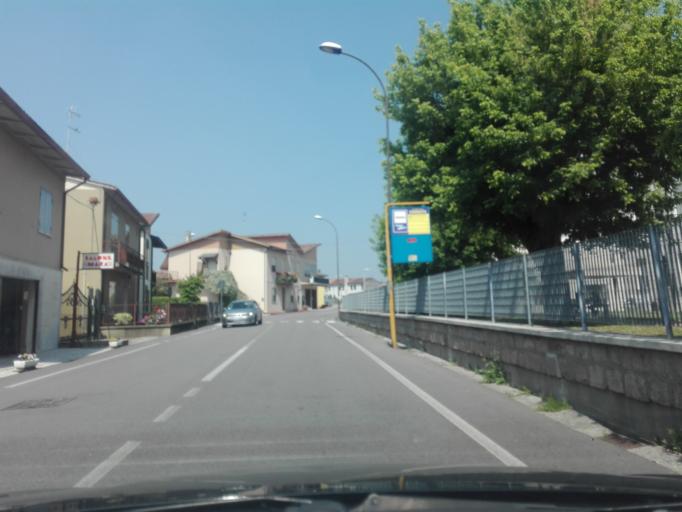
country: IT
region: Veneto
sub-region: Provincia di Rovigo
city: Villadose
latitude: 45.0717
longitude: 11.8949
